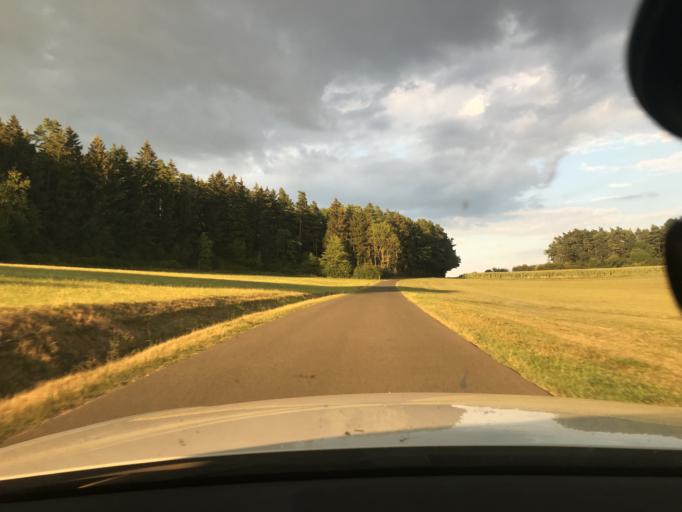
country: DE
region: Bavaria
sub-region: Upper Franconia
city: Pegnitz
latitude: 49.7459
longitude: 11.5715
